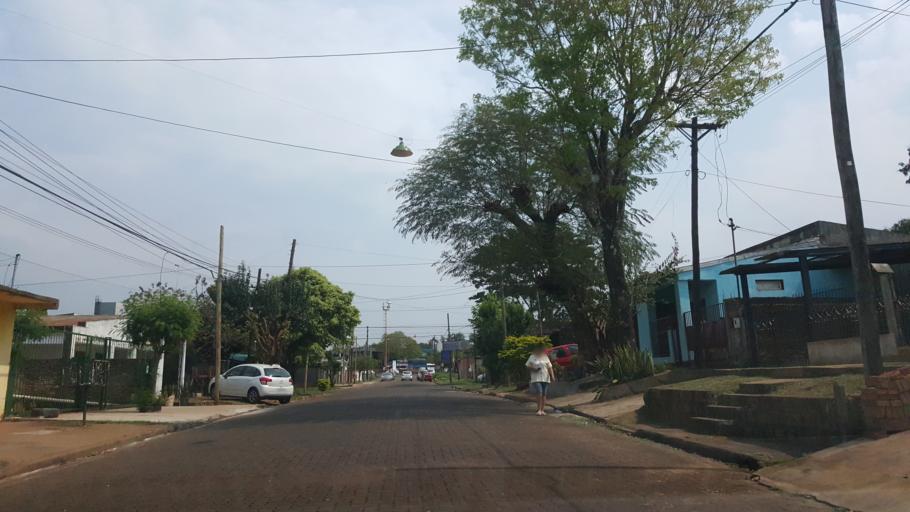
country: AR
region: Misiones
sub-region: Departamento de Capital
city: Posadas
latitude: -27.4017
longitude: -55.9121
